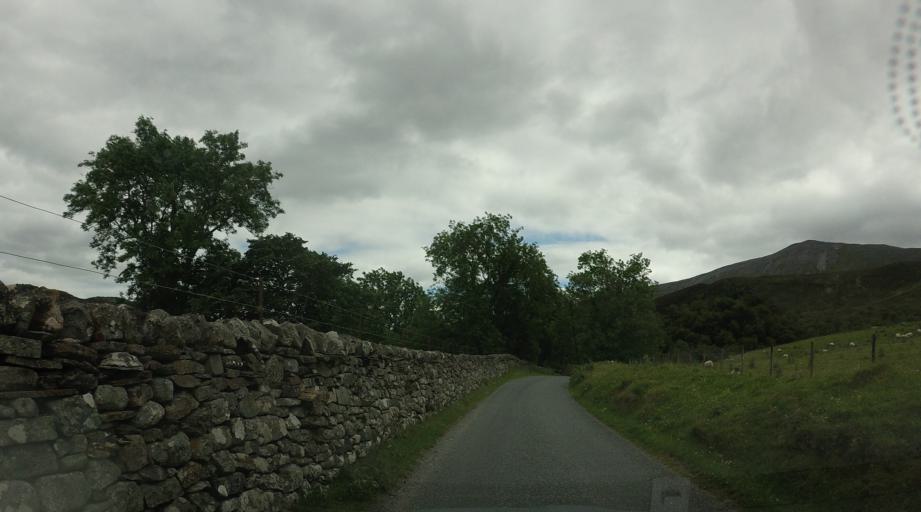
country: GB
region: Scotland
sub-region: Perth and Kinross
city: Aberfeldy
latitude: 56.6926
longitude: -4.1078
